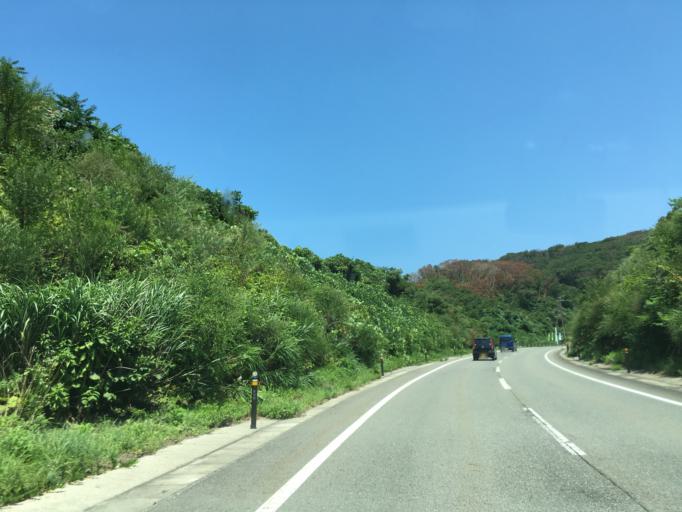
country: JP
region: Akita
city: Tenno
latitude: 39.9605
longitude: 139.7229
